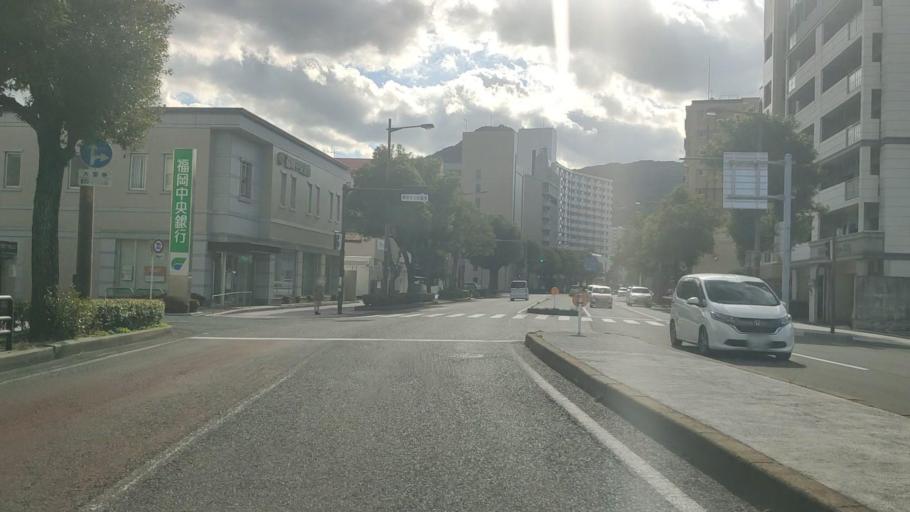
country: JP
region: Yamaguchi
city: Shimonoseki
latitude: 33.9489
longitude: 130.9671
